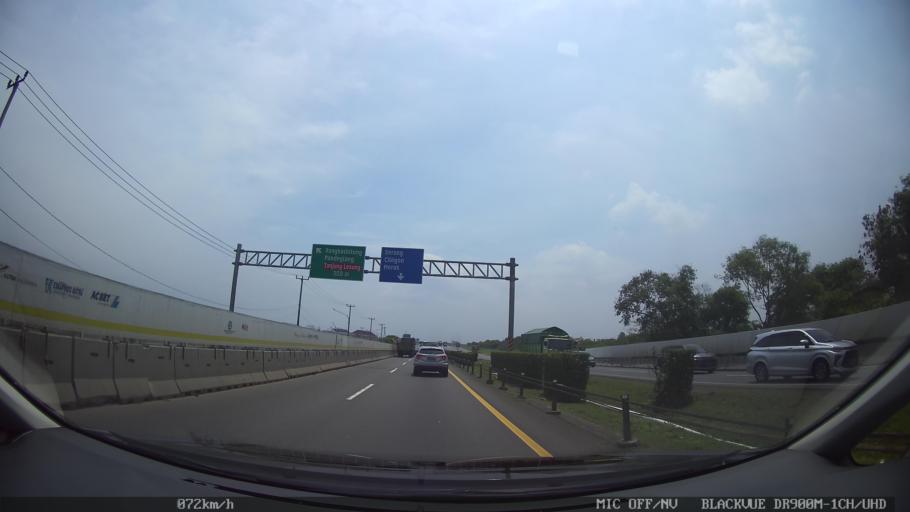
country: ID
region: Banten
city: Serang
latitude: -6.1389
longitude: 106.2562
